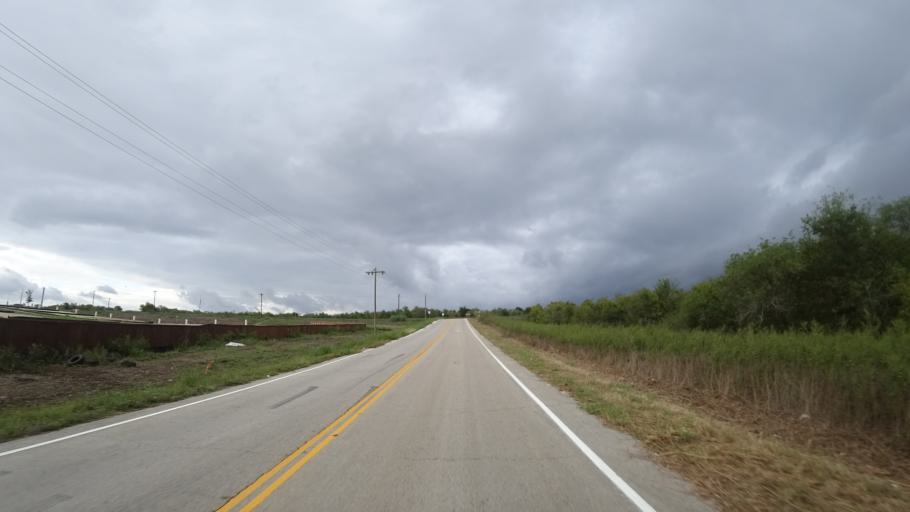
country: US
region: Texas
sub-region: Travis County
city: Onion Creek
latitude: 30.1577
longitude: -97.7316
